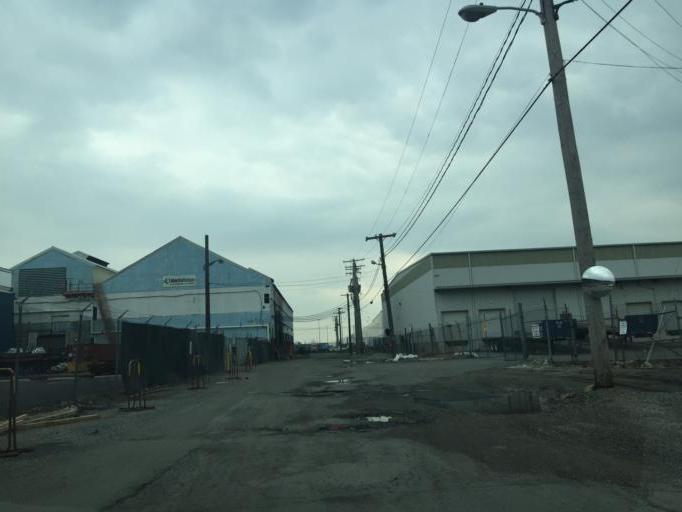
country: US
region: Maryland
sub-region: Baltimore County
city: Dundalk
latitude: 39.2738
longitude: -76.5616
